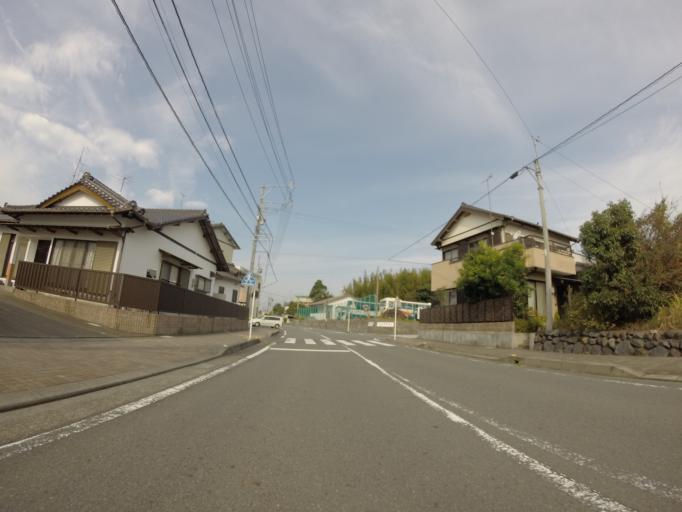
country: JP
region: Shizuoka
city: Sagara
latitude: 34.7441
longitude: 138.2234
